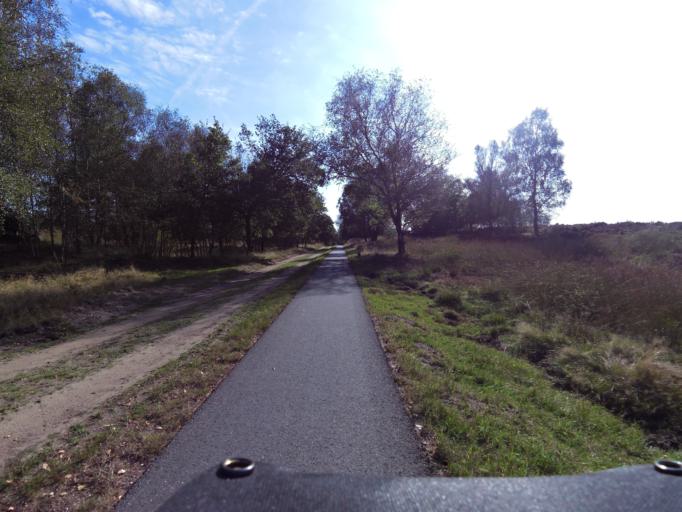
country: NL
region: Gelderland
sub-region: Gemeente Apeldoorn
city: Uddel
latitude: 52.1992
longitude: 5.8609
